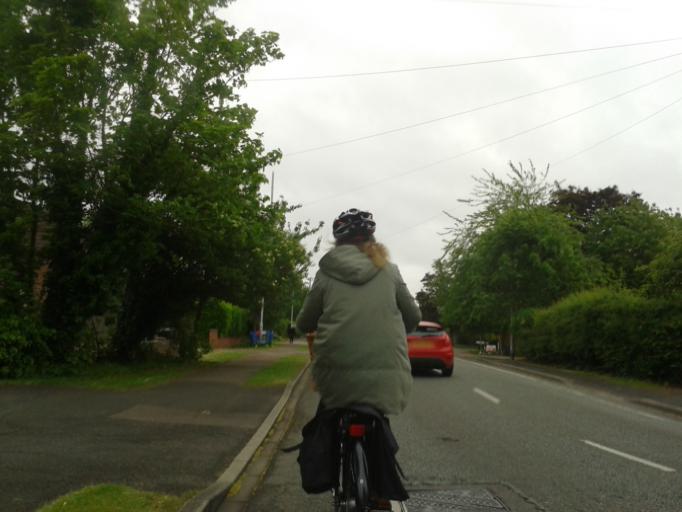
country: GB
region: England
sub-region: Cambridgeshire
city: Cambridge
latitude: 52.2256
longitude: 0.1120
